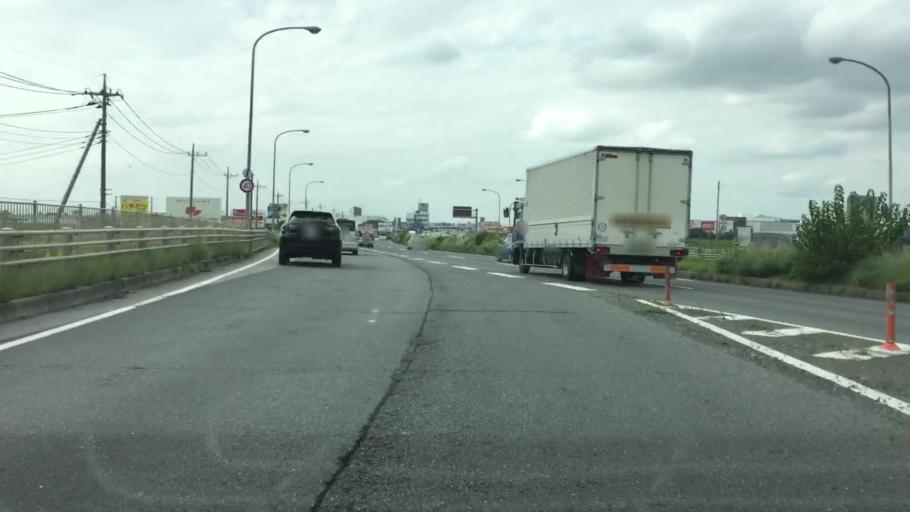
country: JP
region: Tochigi
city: Sano
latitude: 36.2953
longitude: 139.6142
